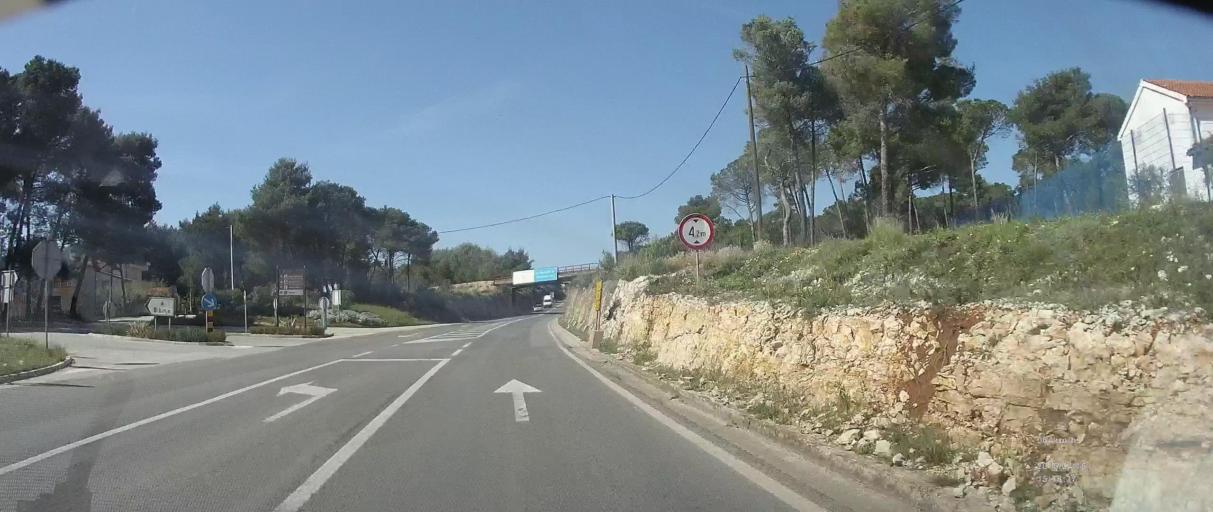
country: HR
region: Zadarska
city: Bibinje
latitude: 44.0621
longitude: 15.2956
